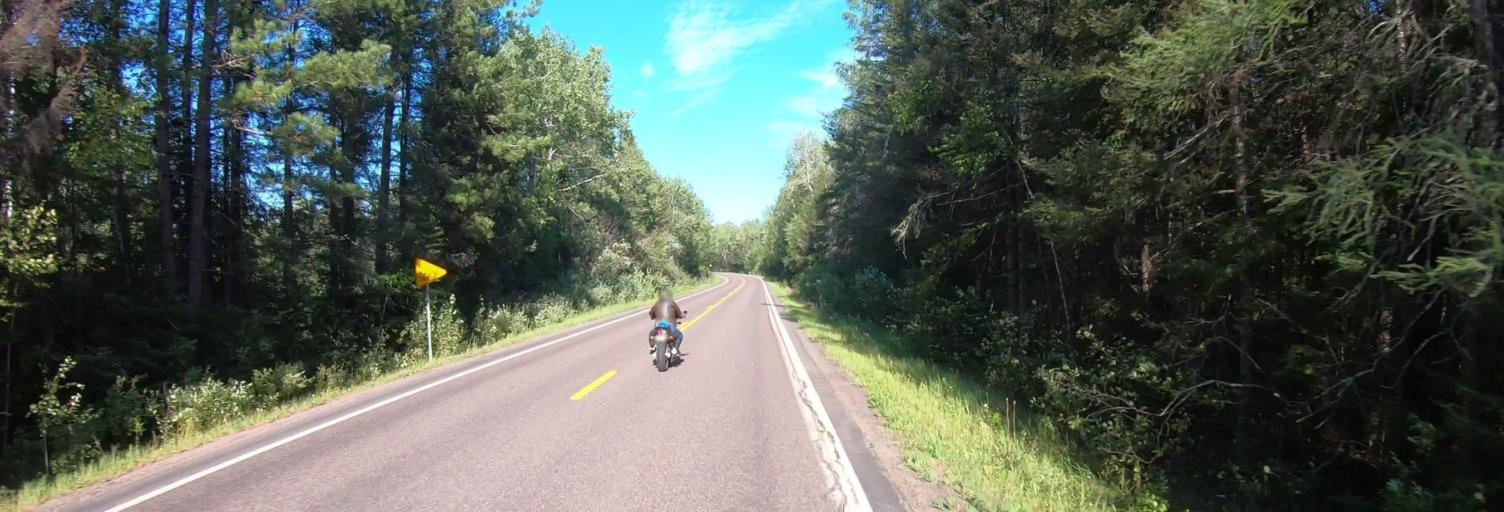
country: US
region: Minnesota
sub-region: Saint Louis County
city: Ely
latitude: 47.9344
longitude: -91.6930
